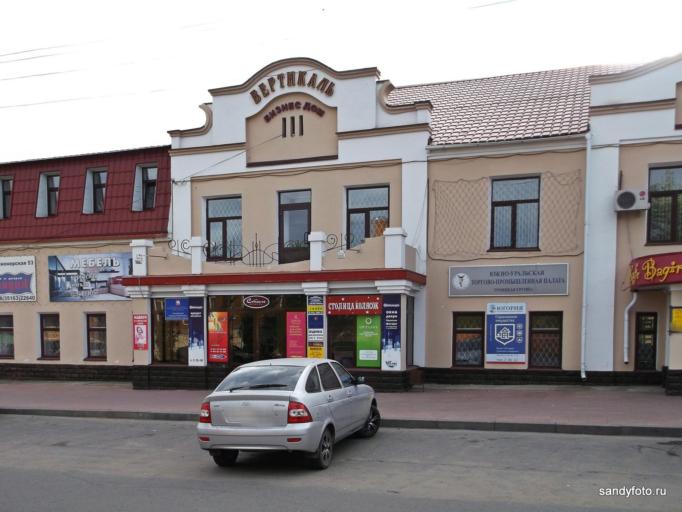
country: RU
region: Chelyabinsk
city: Troitsk
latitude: 54.0836
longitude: 61.5468
